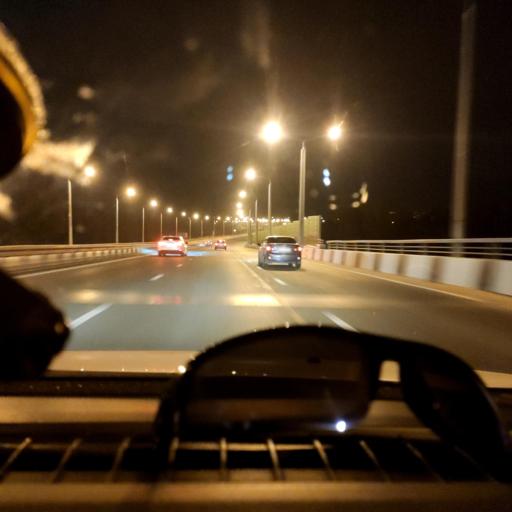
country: RU
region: Samara
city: Rozhdestveno
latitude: 53.1729
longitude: 50.0858
